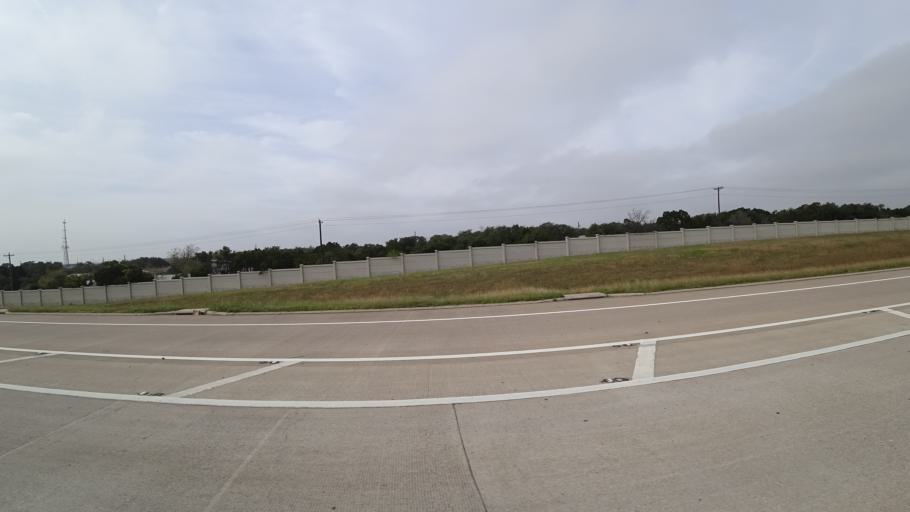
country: US
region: Texas
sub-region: Williamson County
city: Cedar Park
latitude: 30.5068
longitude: -97.8103
